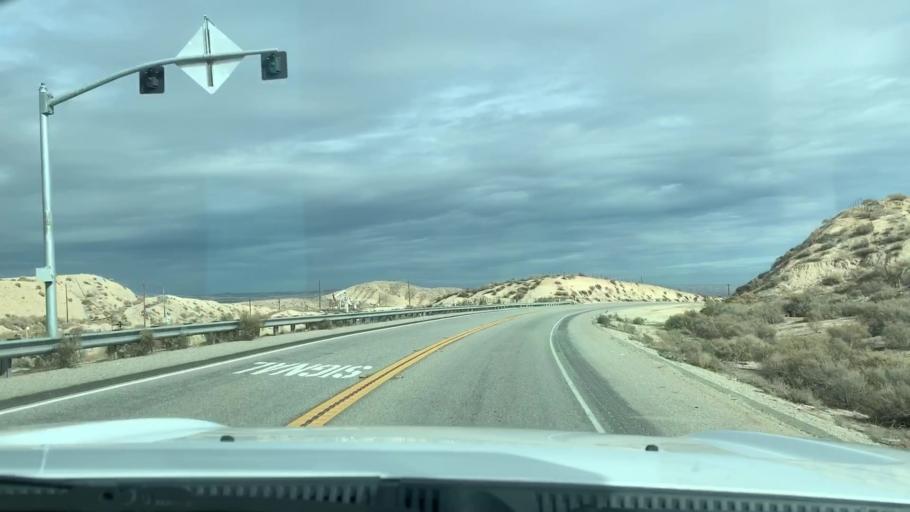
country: US
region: California
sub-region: Kern County
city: Ford City
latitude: 35.1833
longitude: -119.4530
